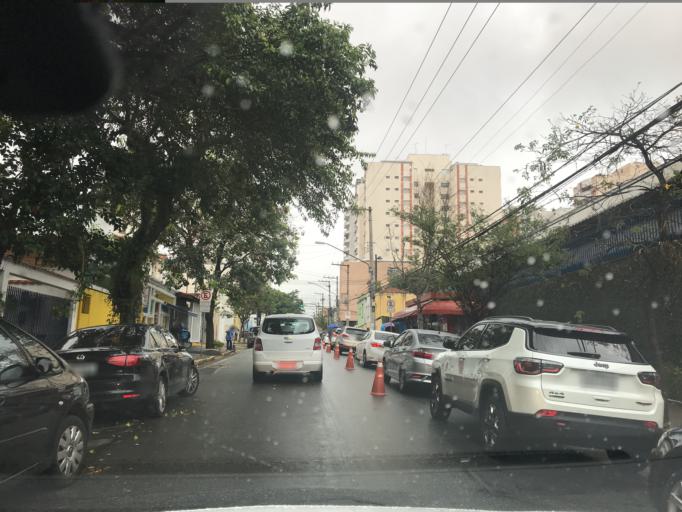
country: BR
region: Sao Paulo
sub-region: Sao Paulo
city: Sao Paulo
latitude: -23.5349
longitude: -46.6842
